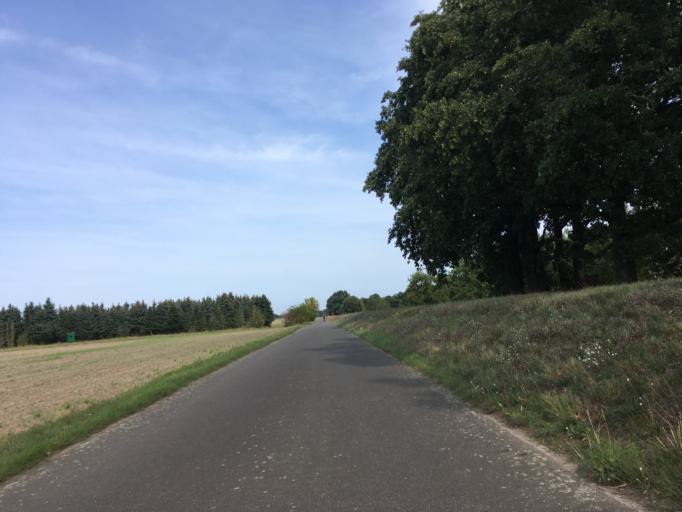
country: DE
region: Brandenburg
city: Guben
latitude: 51.9831
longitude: 14.7126
